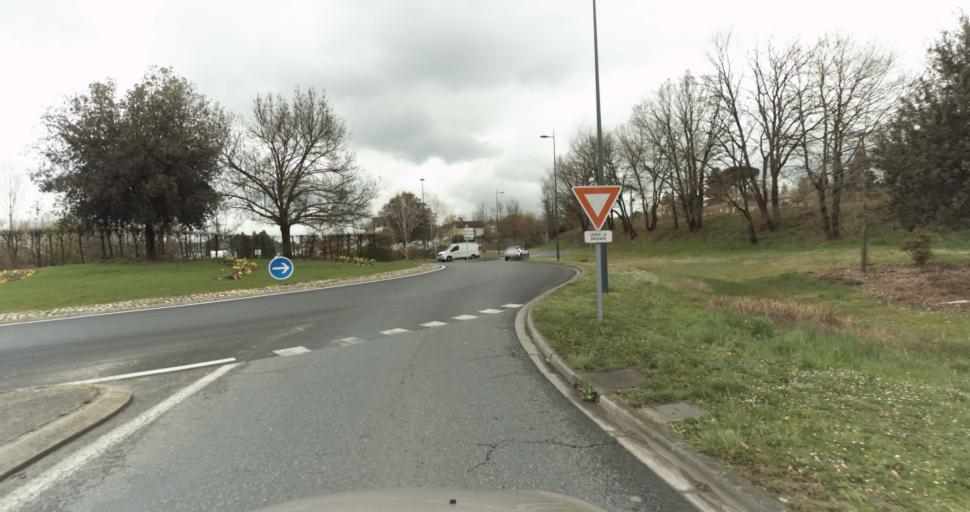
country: FR
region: Midi-Pyrenees
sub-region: Departement du Tarn
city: Puygouzon
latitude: 43.8988
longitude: 2.1491
